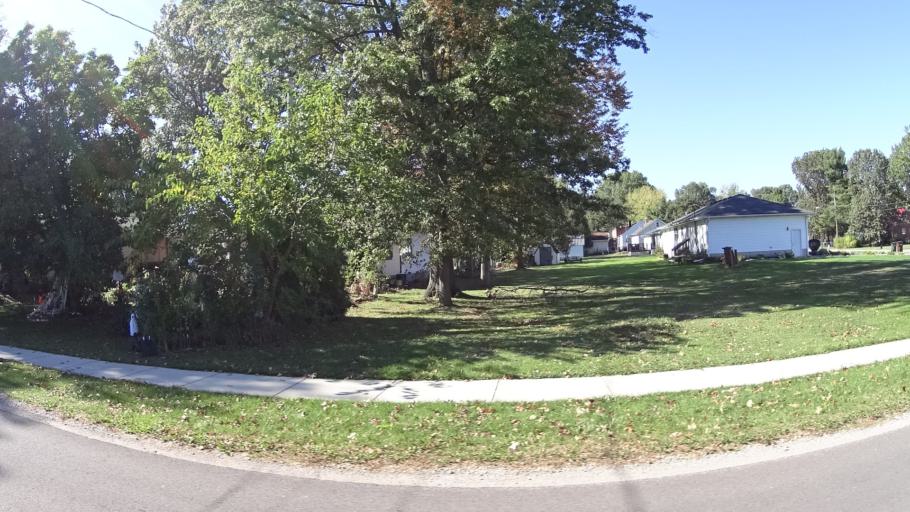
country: US
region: Ohio
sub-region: Lorain County
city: Lorain
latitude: 41.4306
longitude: -82.1587
